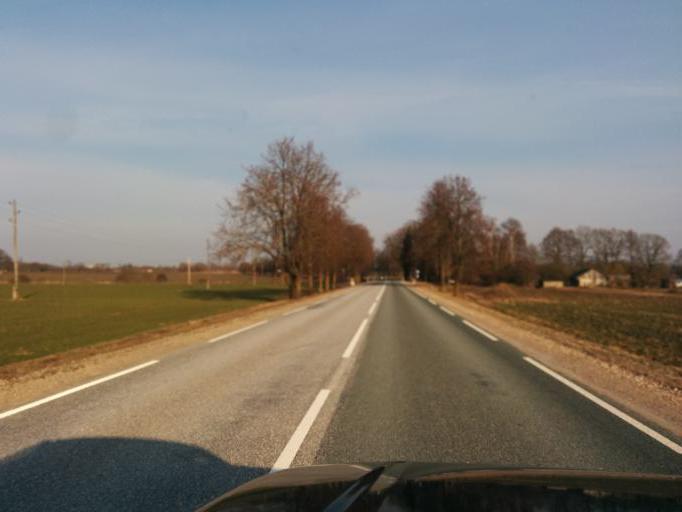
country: LV
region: Lecava
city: Iecava
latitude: 56.5891
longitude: 24.1447
